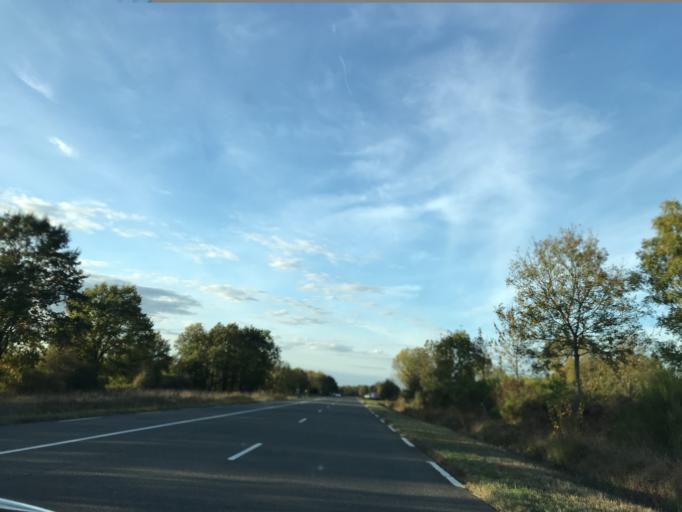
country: FR
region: Auvergne
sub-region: Departement de l'Allier
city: Saint-Yorre
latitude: 46.0200
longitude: 3.4815
